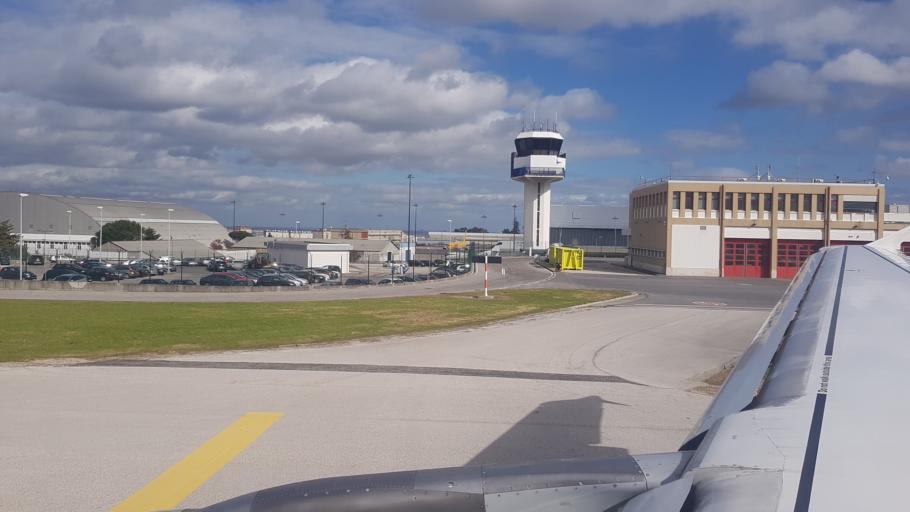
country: PT
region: Lisbon
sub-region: Loures
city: Camarate
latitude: 38.7815
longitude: -9.1334
